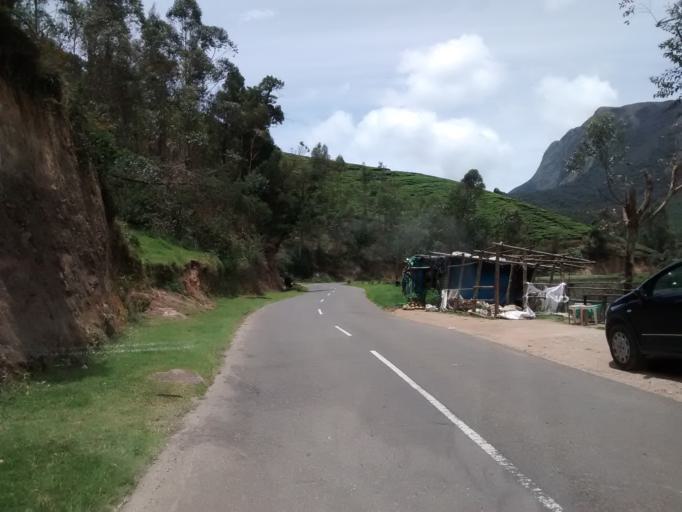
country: IN
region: Kerala
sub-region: Idukki
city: Munnar
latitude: 10.1301
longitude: 77.2044
